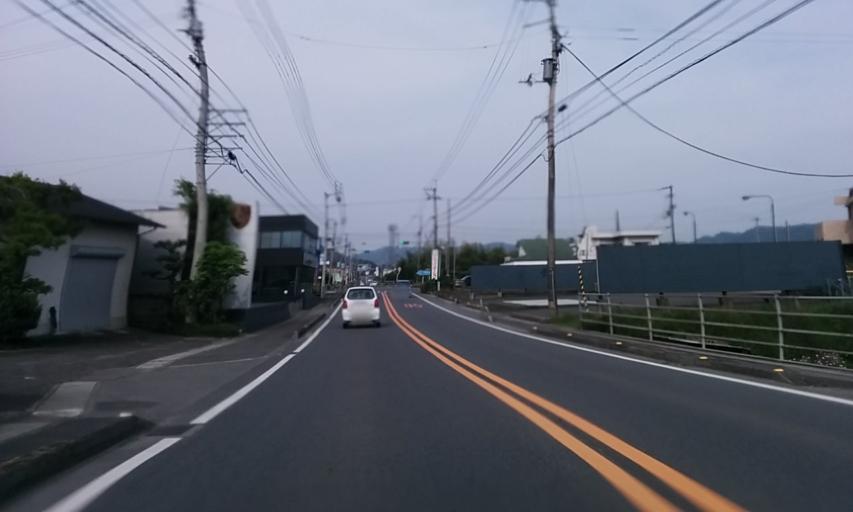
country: JP
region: Ehime
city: Niihama
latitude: 33.9535
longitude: 133.4160
